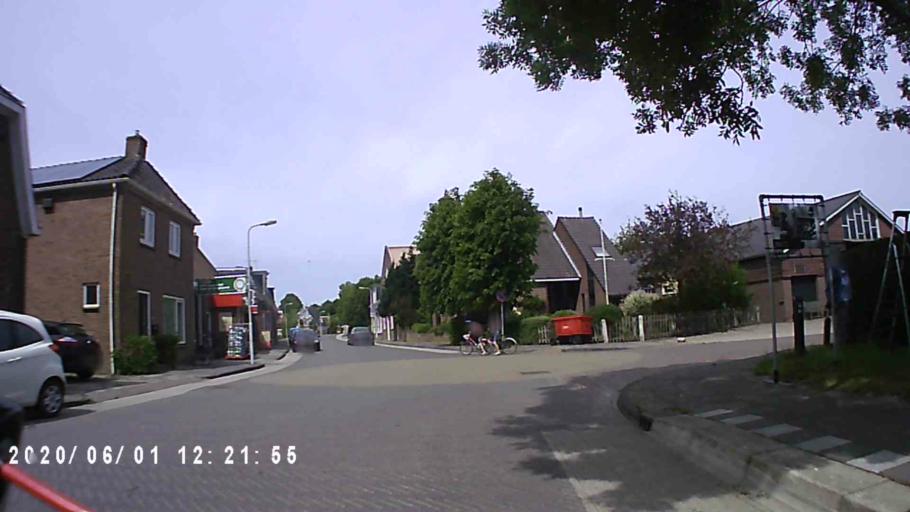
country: NL
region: Friesland
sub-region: Gemeente Harlingen
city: Harlingen
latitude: 53.1289
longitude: 5.4789
